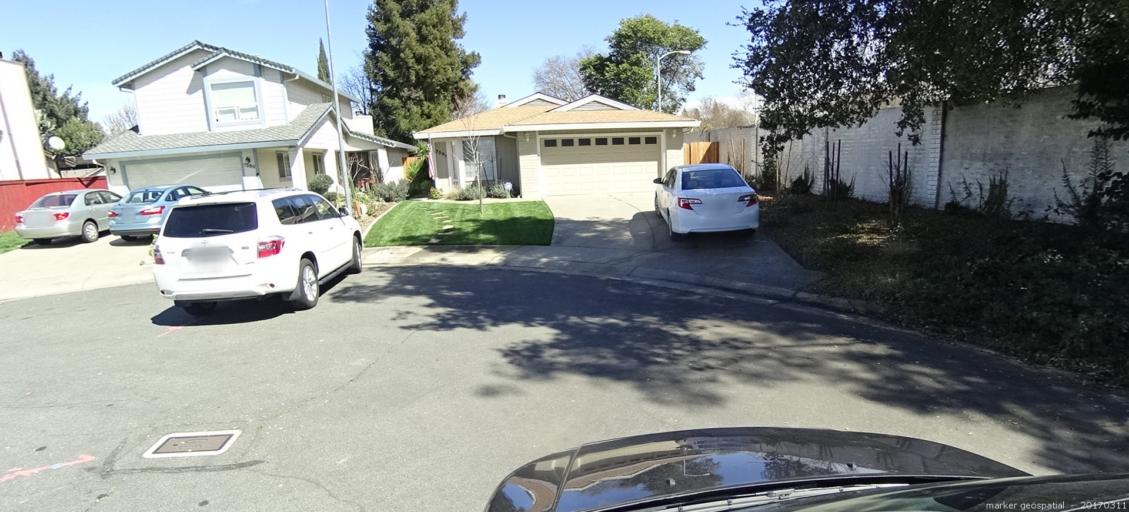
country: US
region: California
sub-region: Sacramento County
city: Parkway
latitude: 38.4793
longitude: -121.5436
